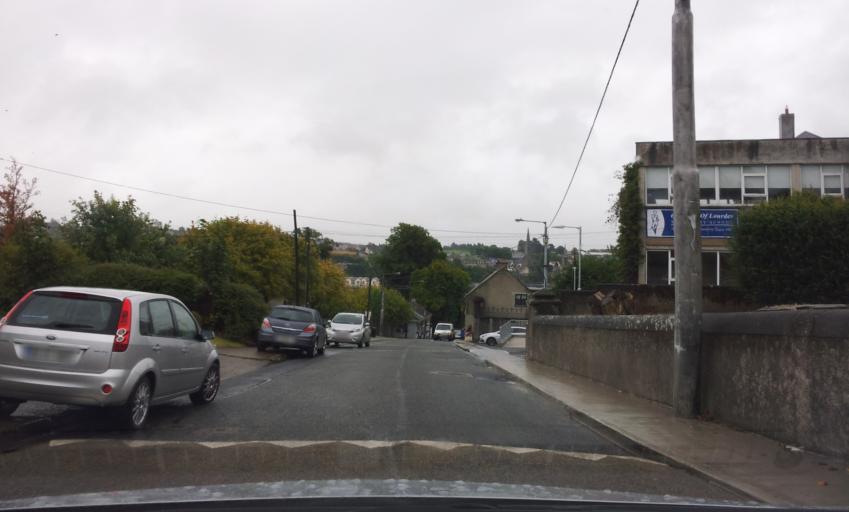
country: IE
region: Leinster
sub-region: Loch Garman
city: New Ross
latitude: 52.3987
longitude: -6.9535
